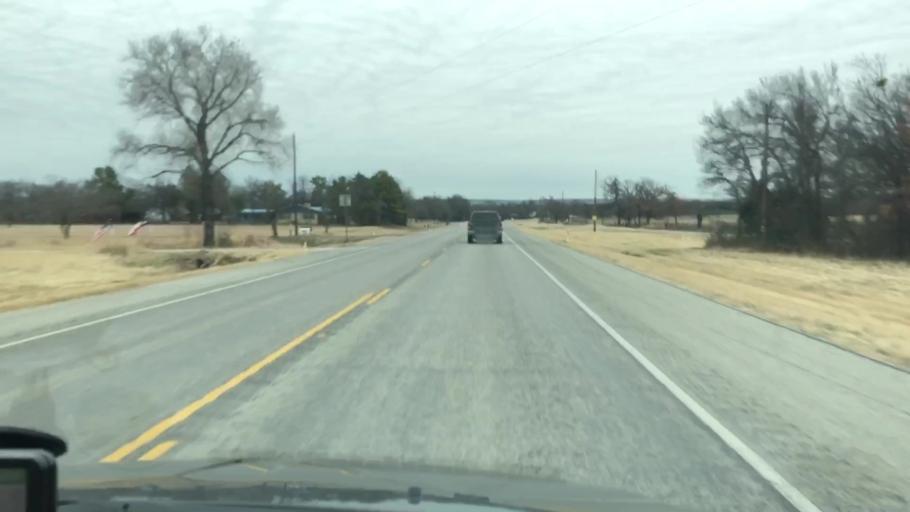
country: US
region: Texas
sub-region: Palo Pinto County
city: Mineral Wells
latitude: 32.8876
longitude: -98.0885
